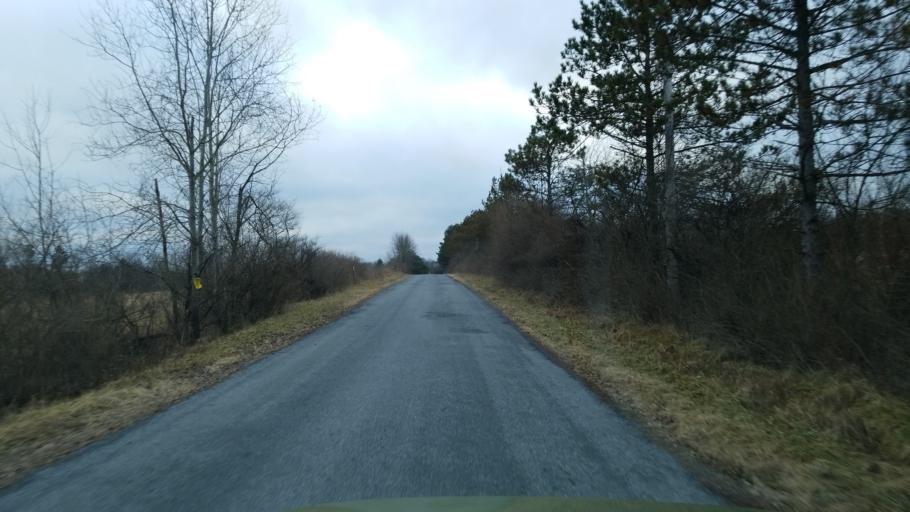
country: US
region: Pennsylvania
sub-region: Jefferson County
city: Falls Creek
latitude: 41.1808
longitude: -78.8060
